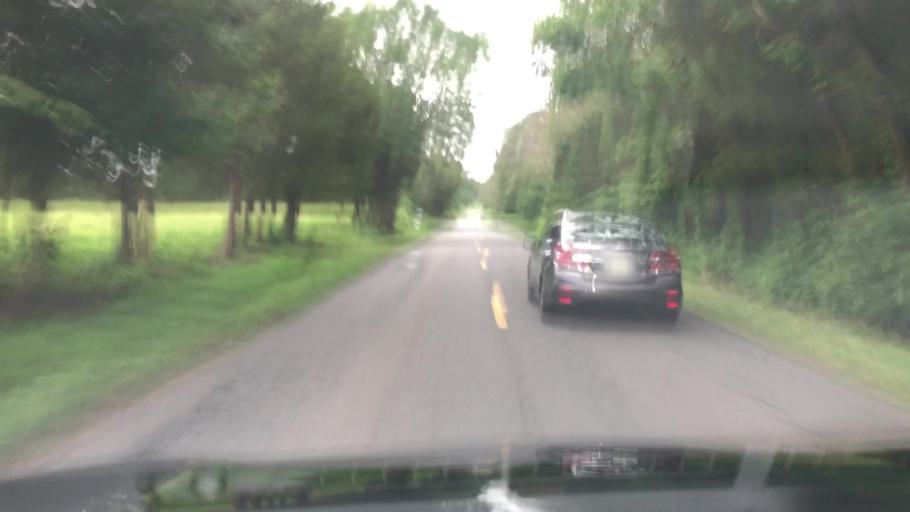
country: US
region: Virginia
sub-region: Prince William County
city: Nokesville
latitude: 38.6767
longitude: -77.6620
